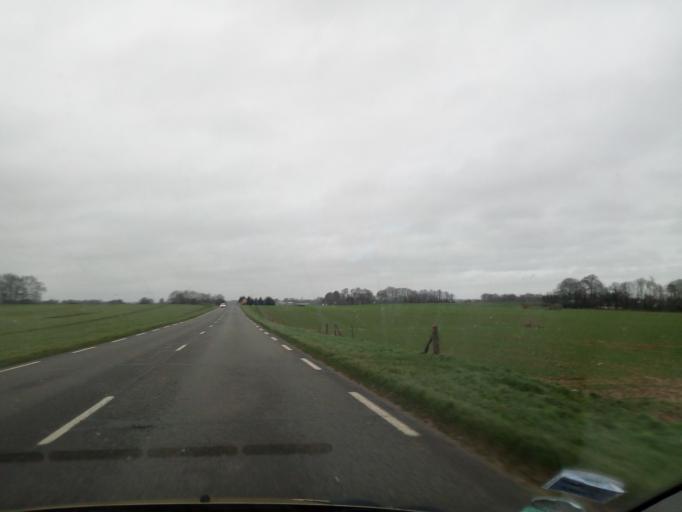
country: FR
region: Haute-Normandie
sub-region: Departement de la Seine-Maritime
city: Auzebosc
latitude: 49.5778
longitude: 0.7289
